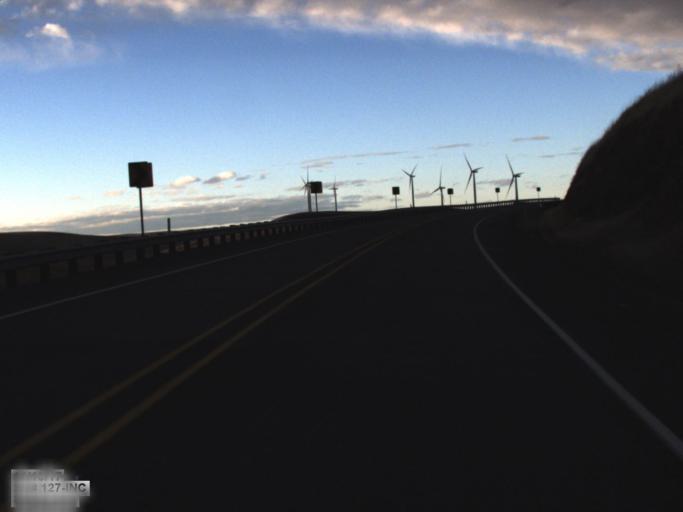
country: US
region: Washington
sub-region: Garfield County
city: Pomeroy
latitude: 46.5664
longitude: -117.7795
